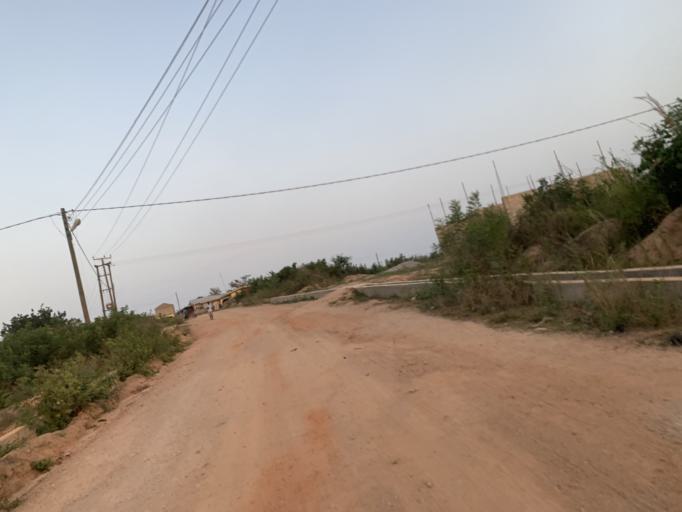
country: GH
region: Central
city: Winneba
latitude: 5.3758
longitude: -0.6080
